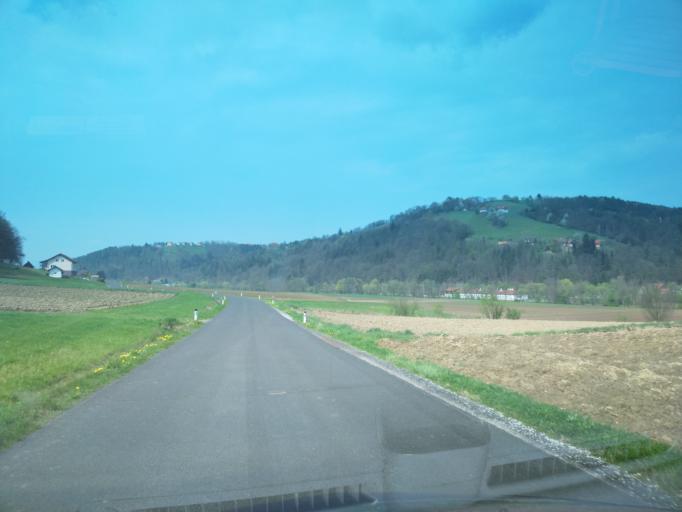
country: AT
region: Styria
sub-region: Politischer Bezirk Leibnitz
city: Kitzeck im Sausal
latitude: 46.7539
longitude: 15.4177
